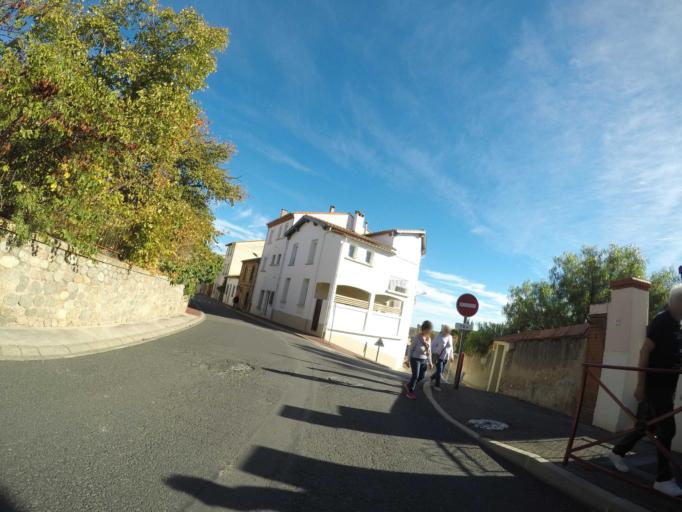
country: FR
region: Languedoc-Roussillon
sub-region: Departement des Pyrenees-Orientales
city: Villemolaque
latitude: 42.5783
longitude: 2.8124
